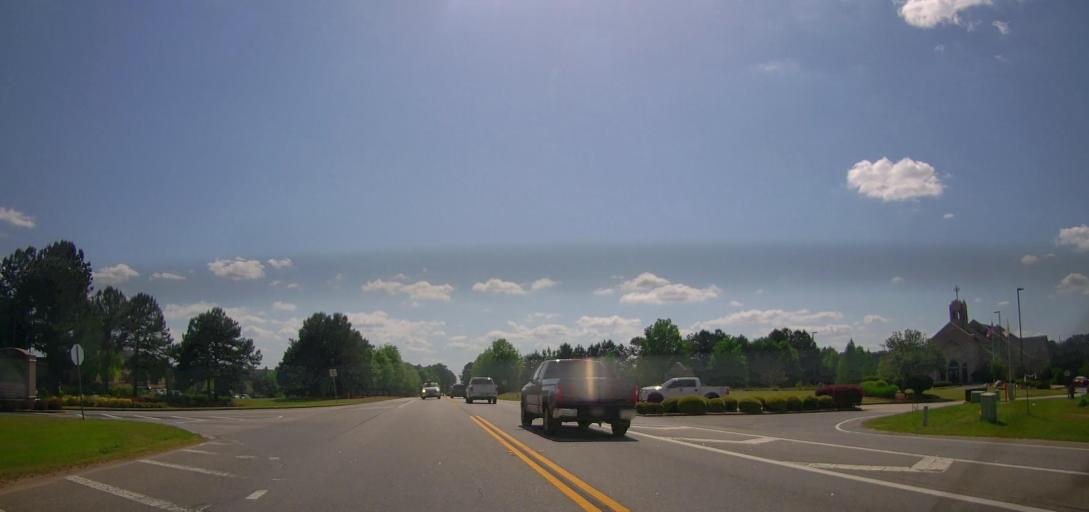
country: US
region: Georgia
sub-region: Putnam County
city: Jefferson
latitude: 33.4570
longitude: -83.2458
